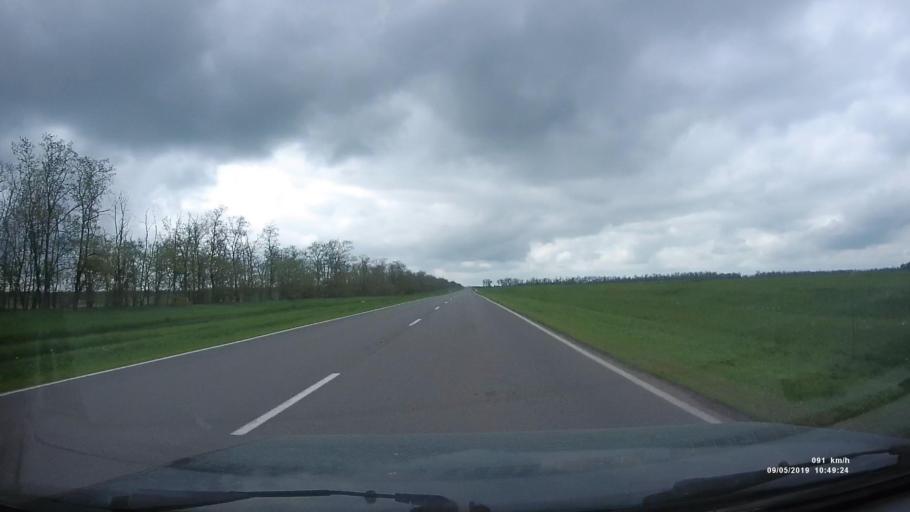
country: RU
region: Rostov
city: Peshkovo
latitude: 46.9431
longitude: 39.3555
